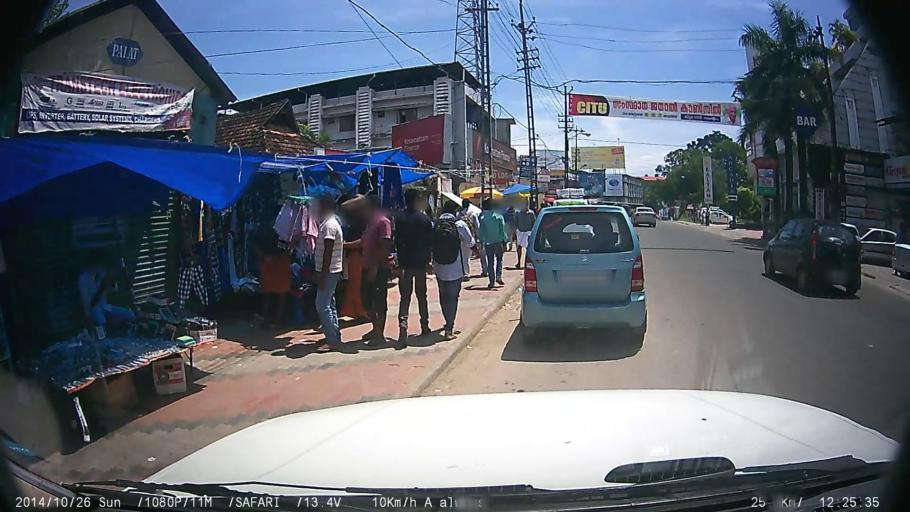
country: IN
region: Kerala
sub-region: Kottayam
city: Kottayam
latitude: 9.5868
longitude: 76.5228
